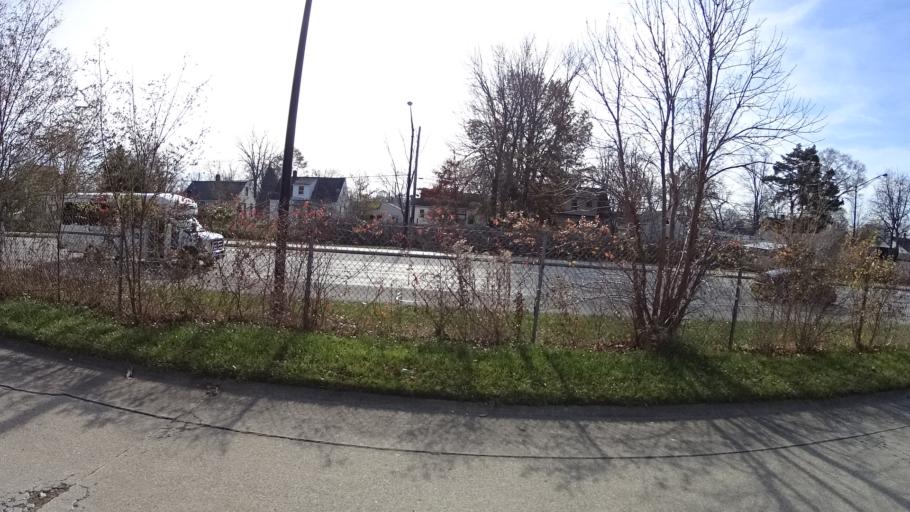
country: US
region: Ohio
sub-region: Lorain County
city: Elyria
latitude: 41.3830
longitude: -82.1095
